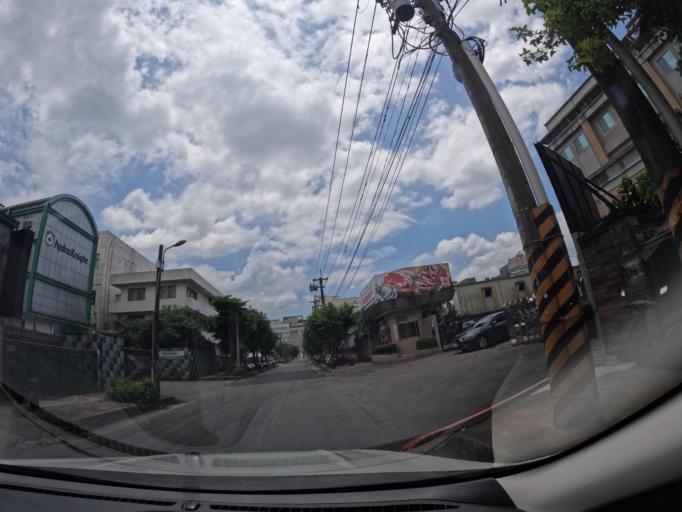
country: TW
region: Taipei
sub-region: Taipei
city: Banqiao
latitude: 24.9664
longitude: 121.4254
